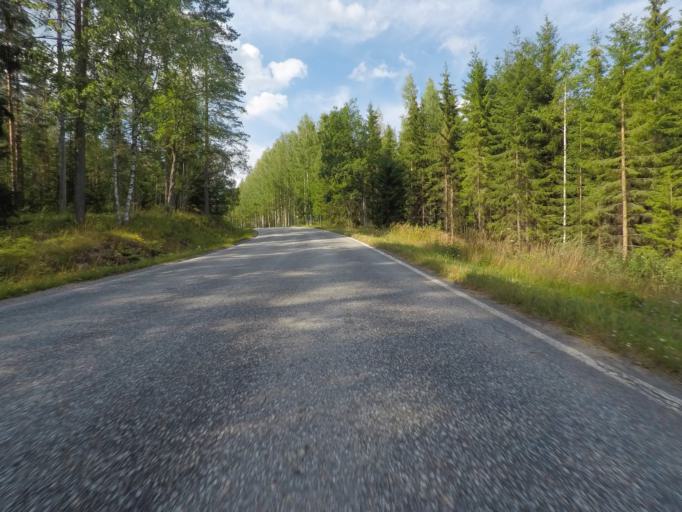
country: FI
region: Southern Savonia
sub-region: Mikkeli
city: Puumala
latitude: 61.6985
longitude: 28.2125
